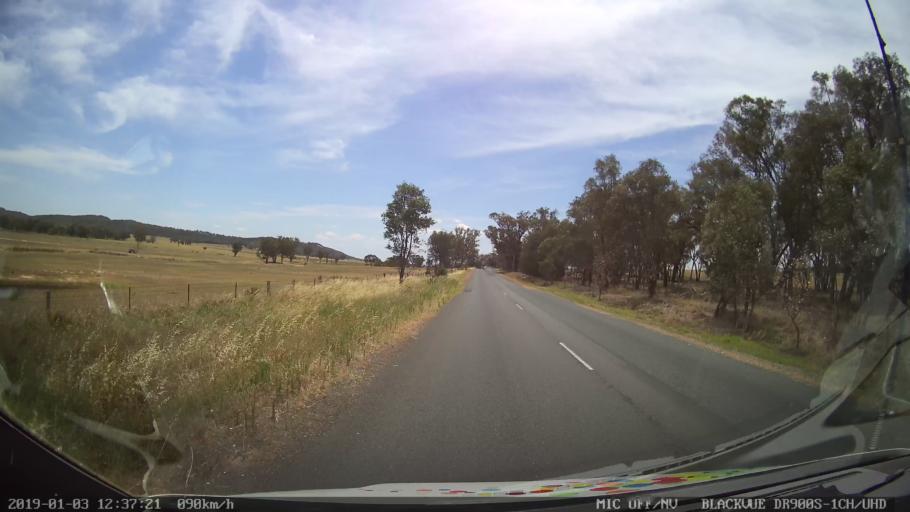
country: AU
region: New South Wales
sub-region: Weddin
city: Grenfell
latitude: -33.8436
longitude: 148.1835
